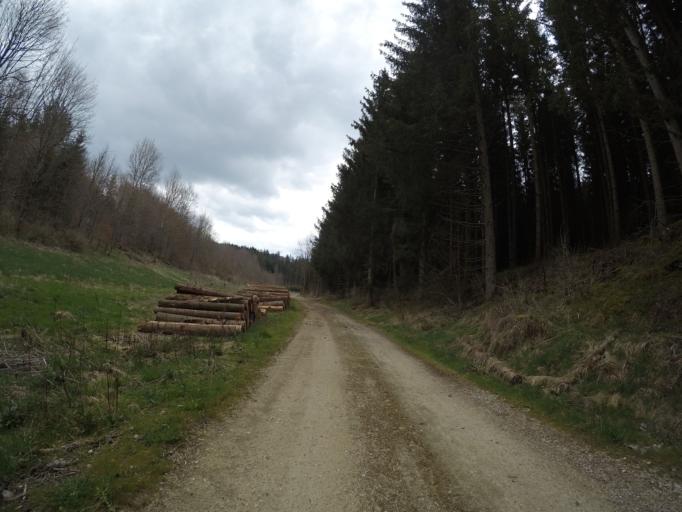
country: DE
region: Baden-Wuerttemberg
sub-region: Tuebingen Region
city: Nellingen
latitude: 48.5009
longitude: 9.7982
